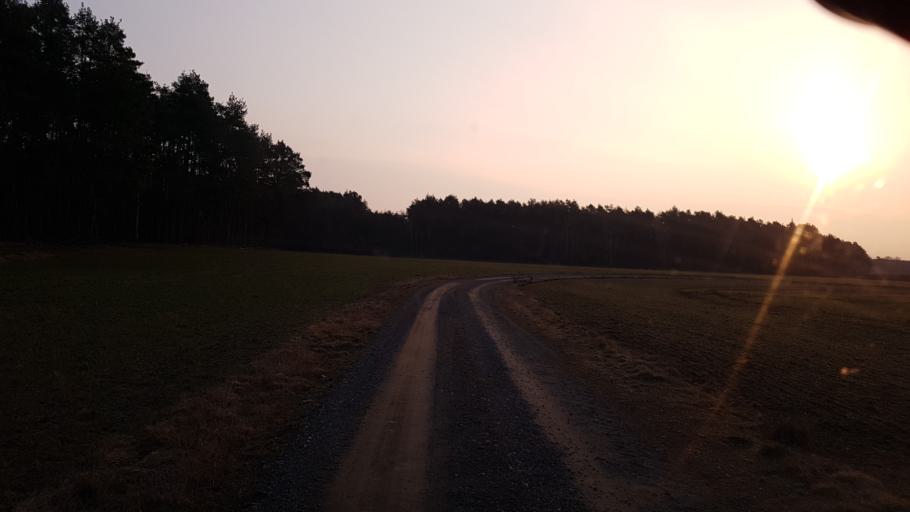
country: DE
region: Brandenburg
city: Falkenberg
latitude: 51.5762
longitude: 13.3054
